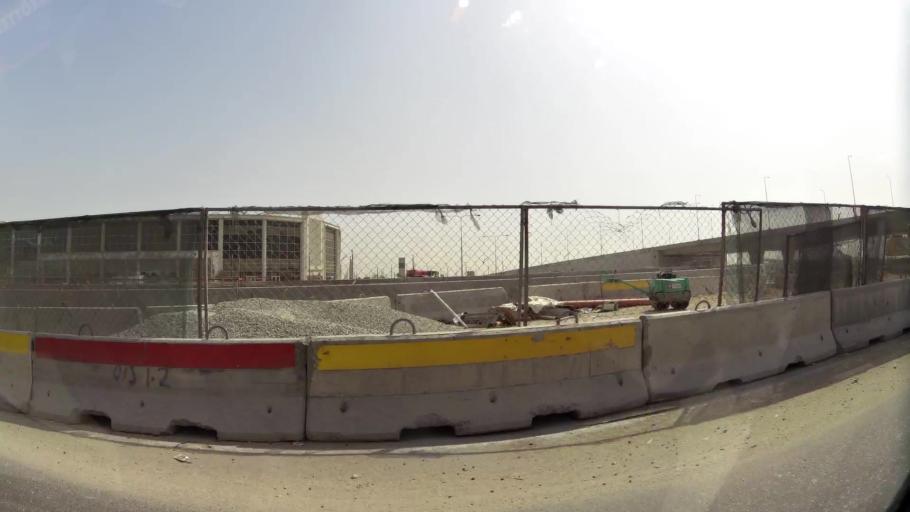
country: QA
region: Al Wakrah
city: Al Wukayr
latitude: 25.1933
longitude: 51.4543
